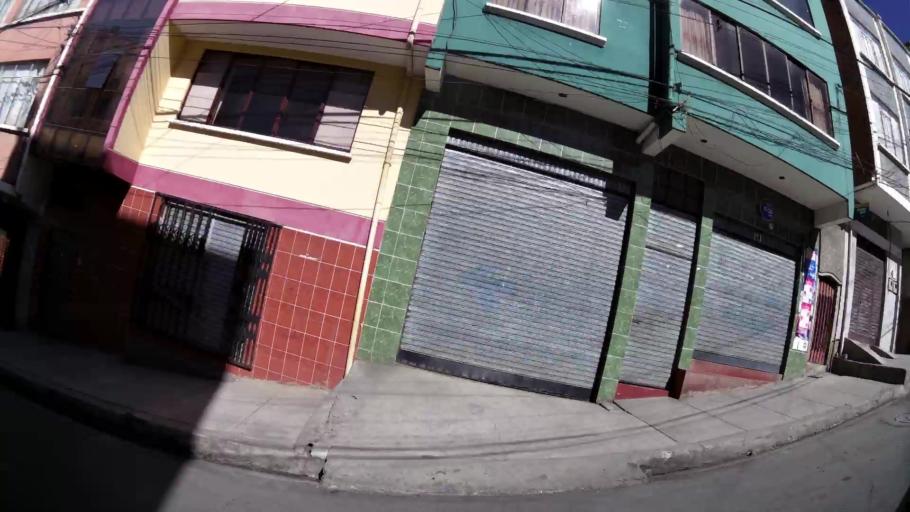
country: BO
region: La Paz
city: La Paz
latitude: -16.5045
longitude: -68.1463
